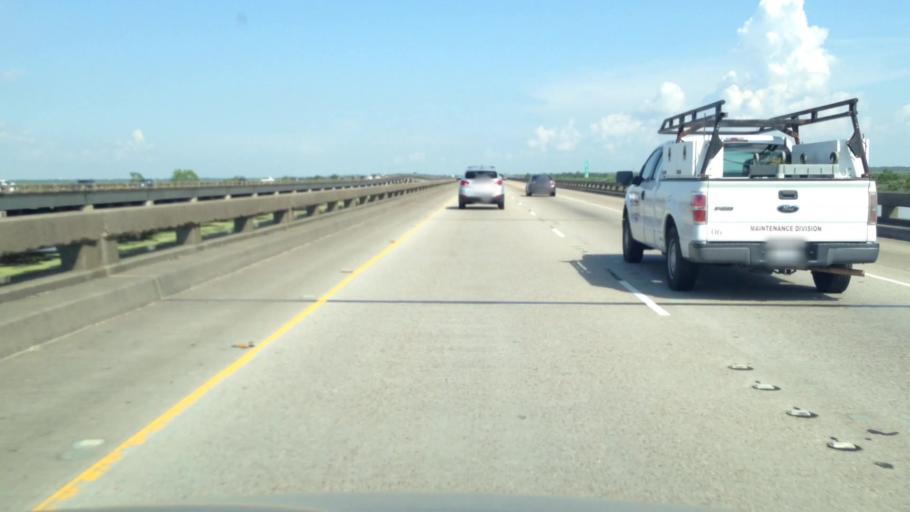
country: US
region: Louisiana
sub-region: Saint Charles Parish
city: New Sarpy
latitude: 30.0303
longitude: -90.3352
